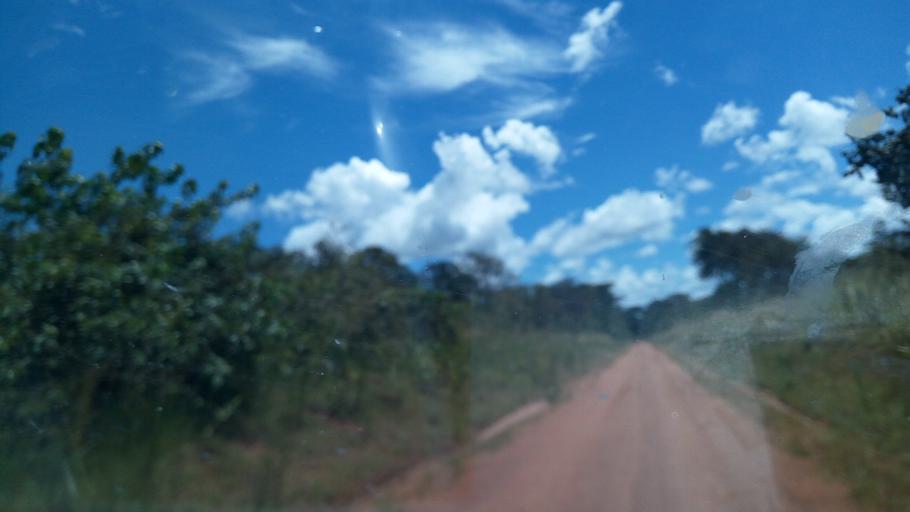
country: CD
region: Katanga
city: Kalemie
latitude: -5.4227
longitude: 28.9356
